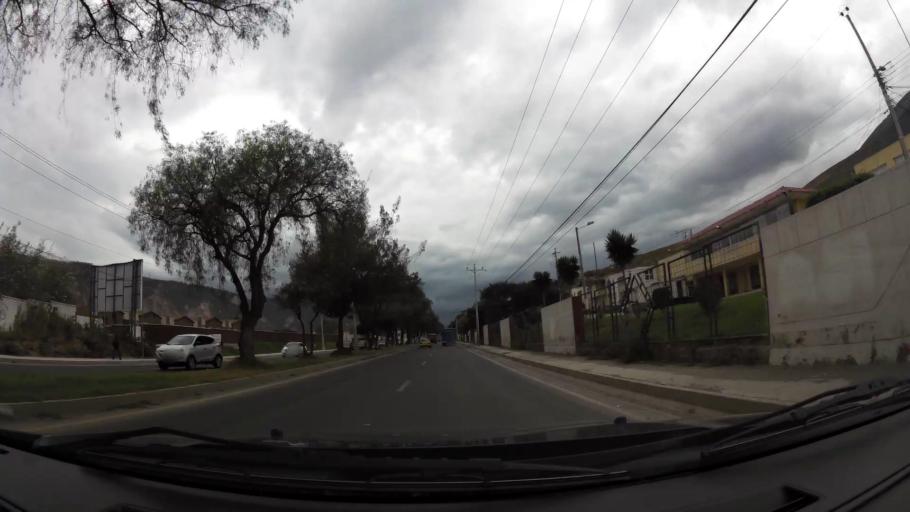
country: EC
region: Pichincha
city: Quito
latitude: -0.0228
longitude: -78.4522
